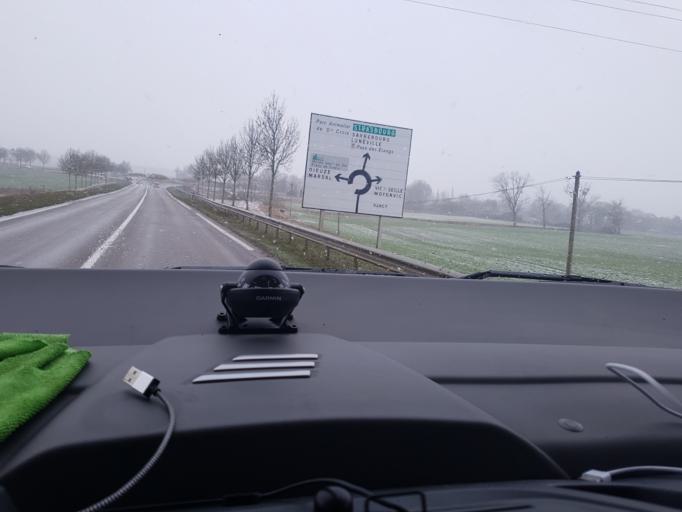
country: FR
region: Lorraine
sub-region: Departement de la Moselle
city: Vic-sur-Seille
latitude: 48.7839
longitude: 6.5672
